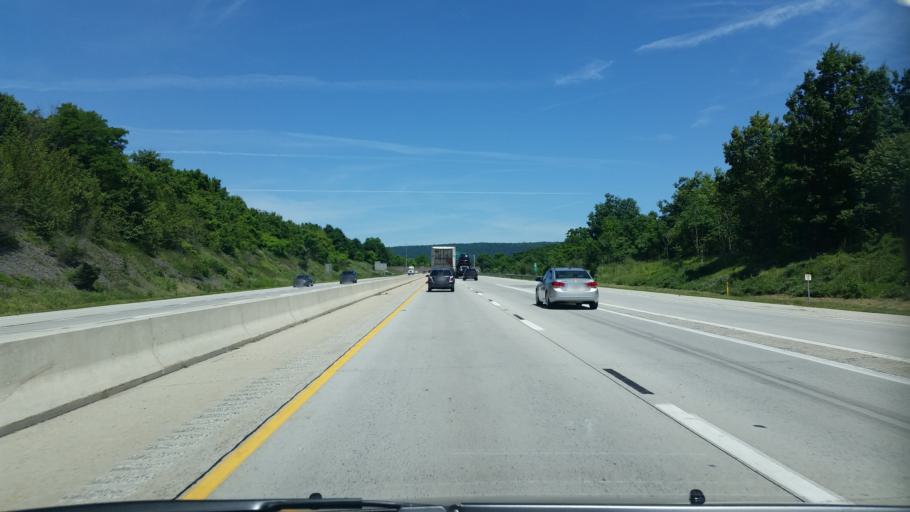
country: US
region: Pennsylvania
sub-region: Cumberland County
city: Mechanicsburg
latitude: 40.2611
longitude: -76.9950
